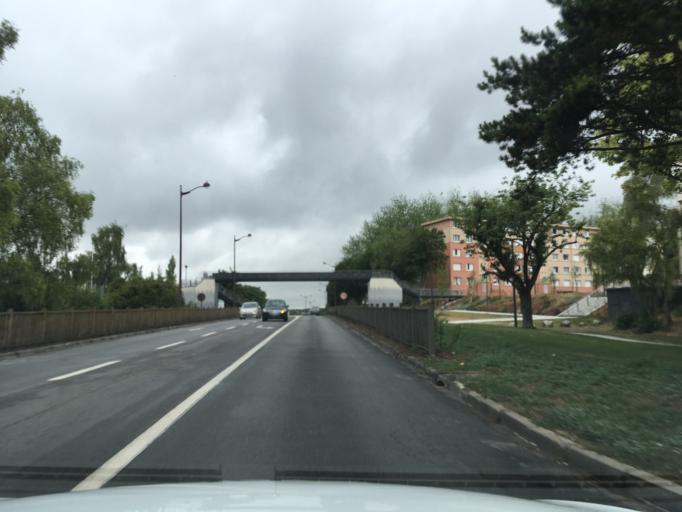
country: FR
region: Picardie
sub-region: Departement de l'Aisne
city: Saint-Quentin
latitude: 49.8505
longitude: 3.2679
